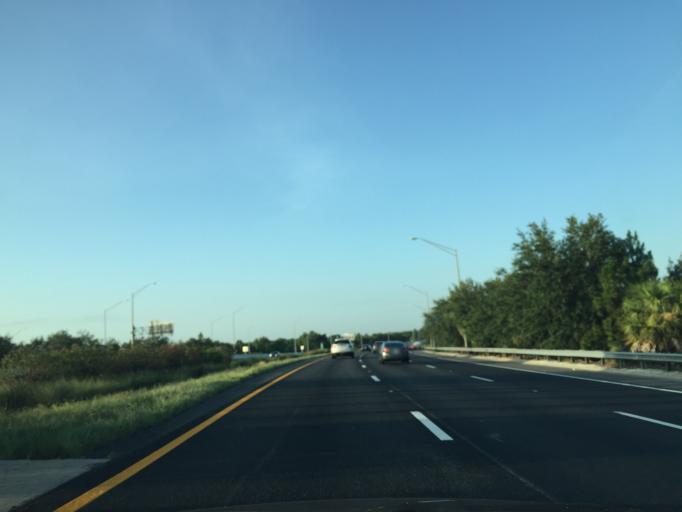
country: US
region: Florida
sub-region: Seminole County
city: Goldenrod
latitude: 28.5973
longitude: -81.2500
